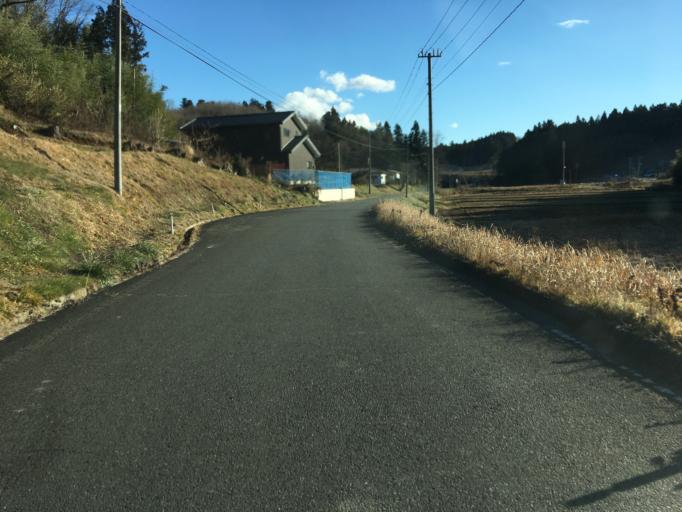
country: JP
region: Fukushima
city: Ishikawa
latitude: 37.2215
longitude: 140.5525
